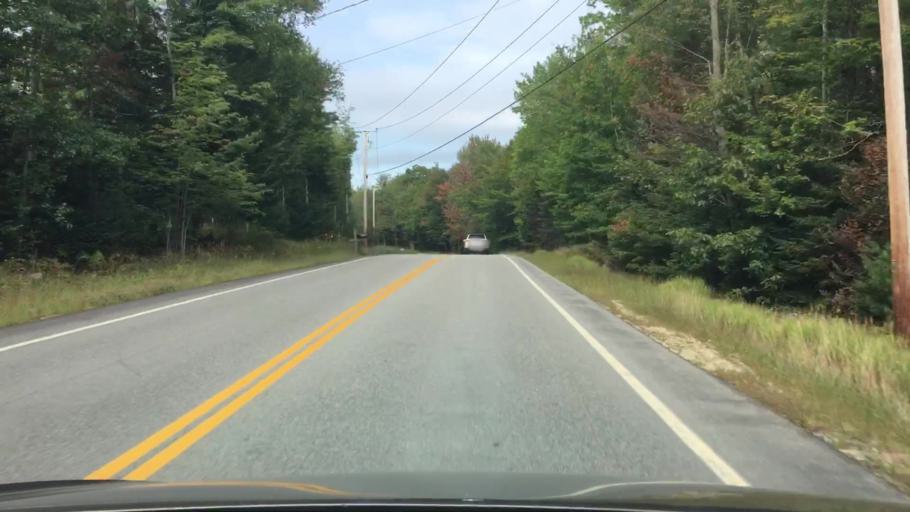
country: US
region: Maine
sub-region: Oxford County
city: Hartford
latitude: 44.3673
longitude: -70.3394
